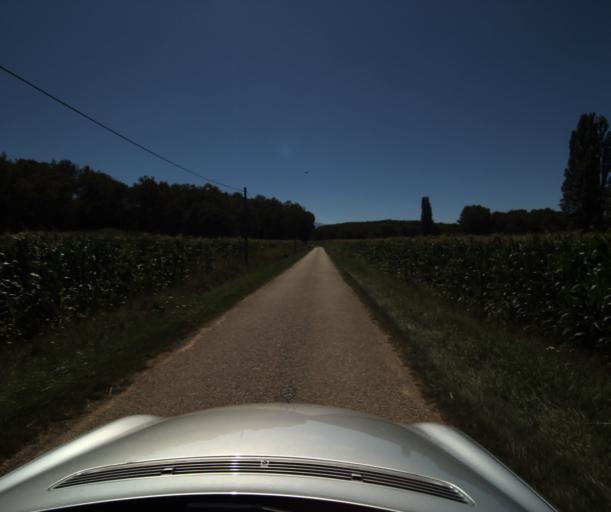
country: FR
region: Midi-Pyrenees
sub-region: Departement de l'Ariege
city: Belesta
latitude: 42.9799
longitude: 1.9148
